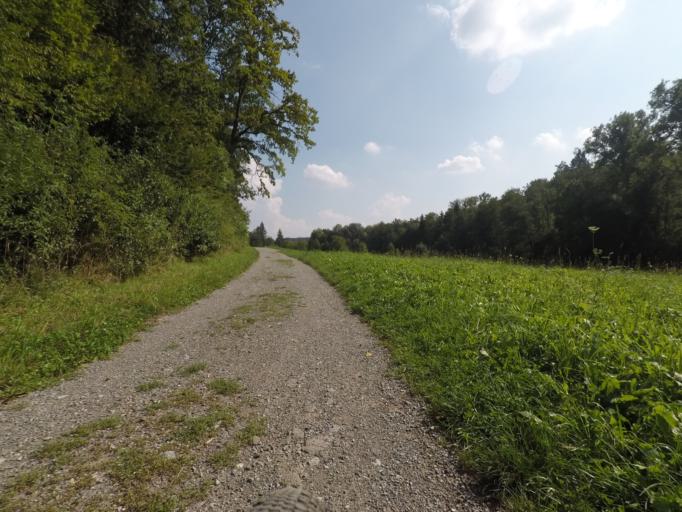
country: DE
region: Baden-Wuerttemberg
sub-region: Regierungsbezirk Stuttgart
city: Steinenbronn
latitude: 48.6954
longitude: 9.1079
